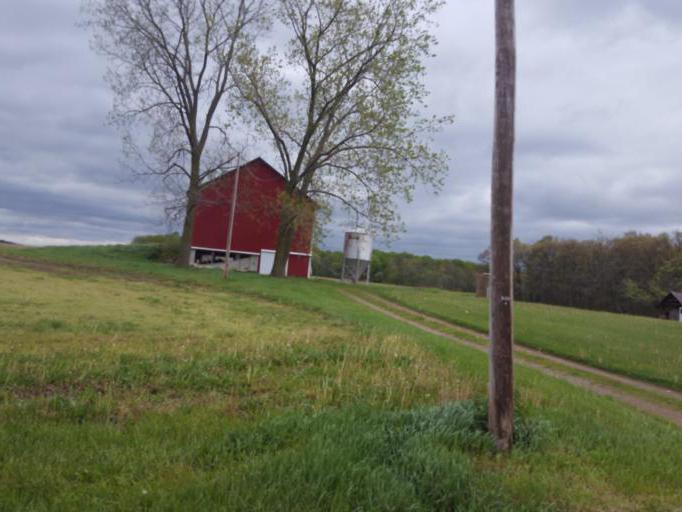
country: US
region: Ohio
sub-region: Sandusky County
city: Bellville
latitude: 40.5504
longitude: -82.5203
